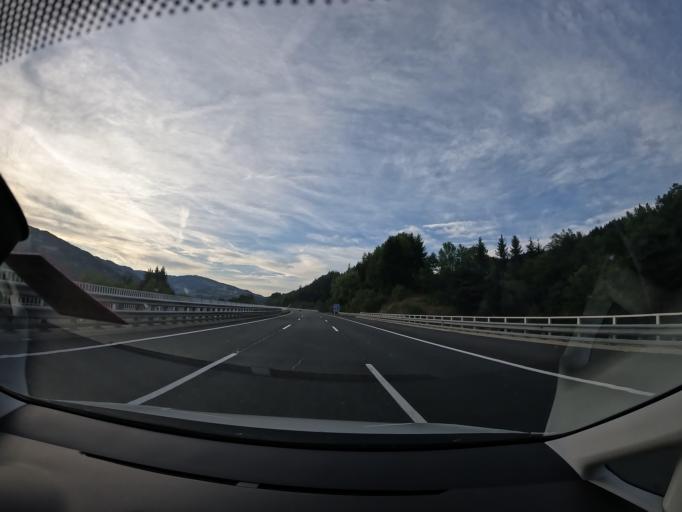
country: AT
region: Carinthia
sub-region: Politischer Bezirk Wolfsberg
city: Wolfsberg
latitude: 46.8838
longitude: 14.8295
